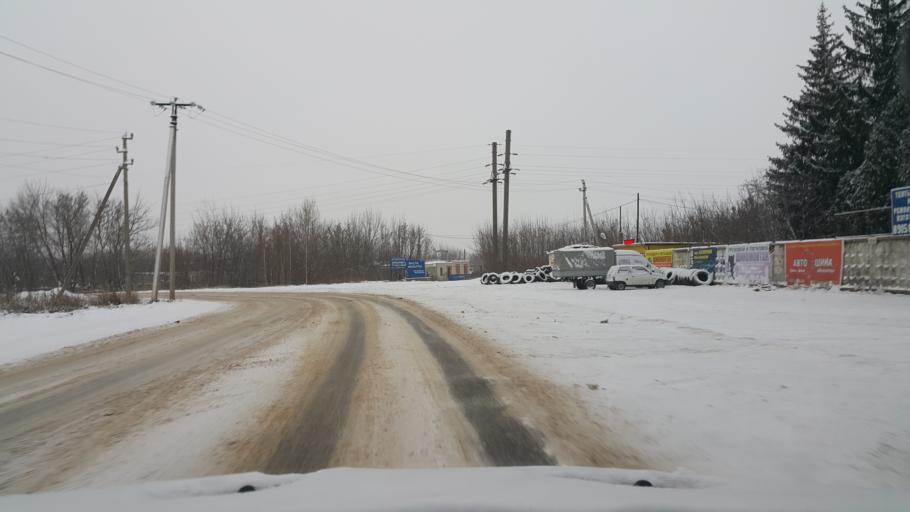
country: RU
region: Tambov
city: Pokrovo-Prigorodnoye
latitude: 52.6556
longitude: 41.4223
